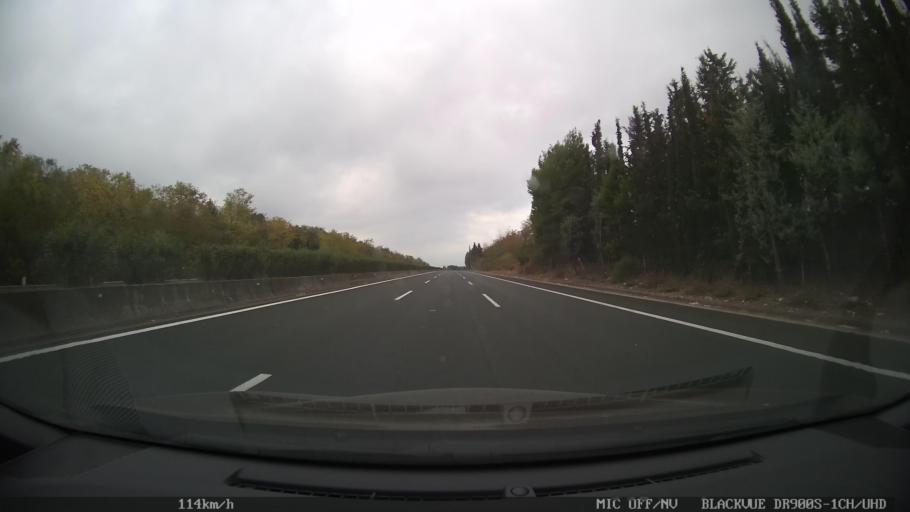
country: GR
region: Central Macedonia
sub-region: Nomos Pierias
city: Kitros
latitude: 40.3506
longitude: 22.5956
